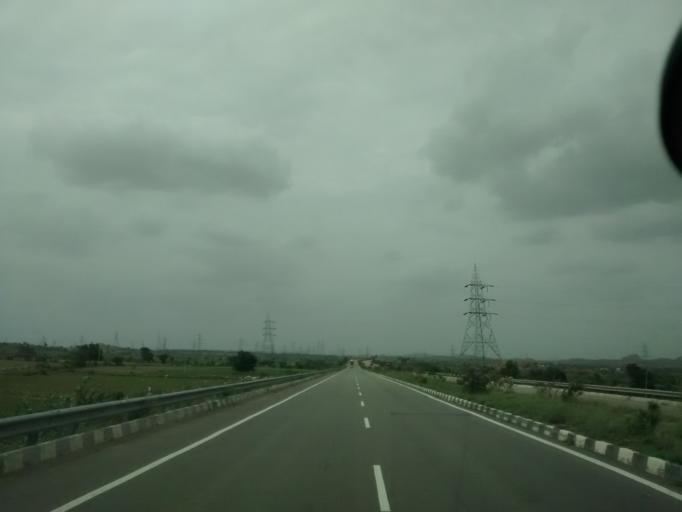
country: IN
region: Andhra Pradesh
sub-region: Kurnool
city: Ramapuram
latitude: 15.1246
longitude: 77.6607
